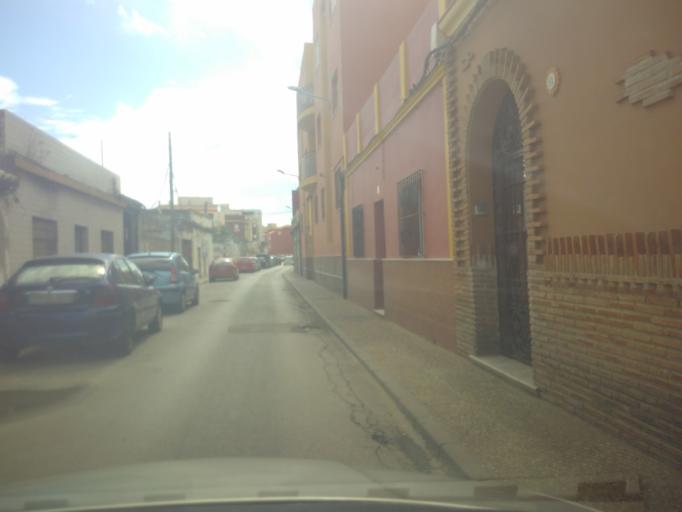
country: ES
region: Andalusia
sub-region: Provincia de Cadiz
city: La Linea de la Concepcion
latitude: 36.1661
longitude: -5.3454
